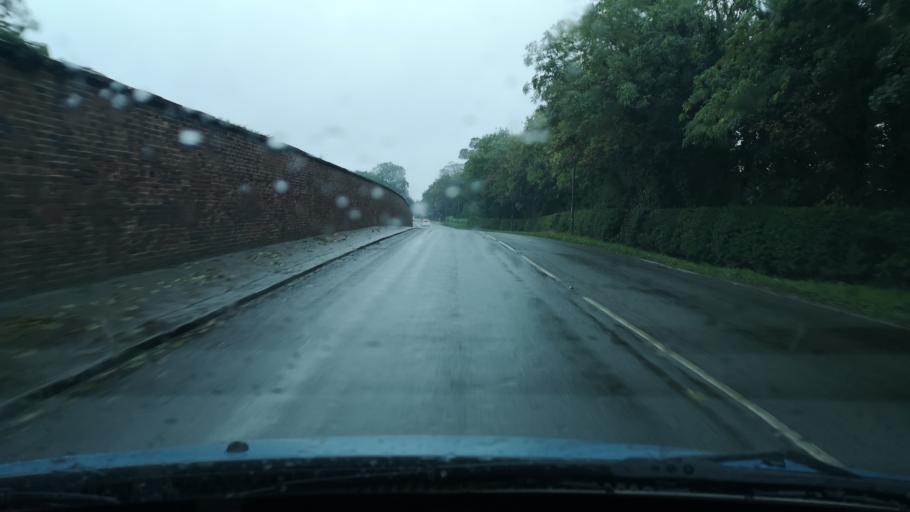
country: GB
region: England
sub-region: City and Borough of Wakefield
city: Fitzwilliam
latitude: 53.6506
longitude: -1.3900
